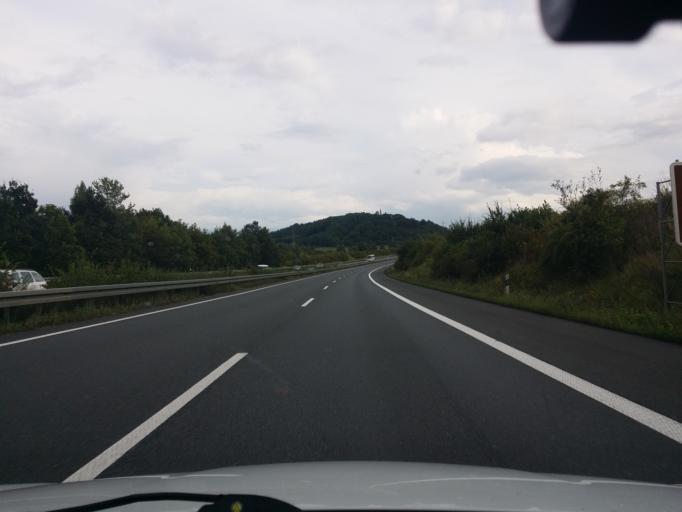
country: DE
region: Lower Saxony
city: Gemeinde Friedland
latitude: 51.4232
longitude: 9.8970
